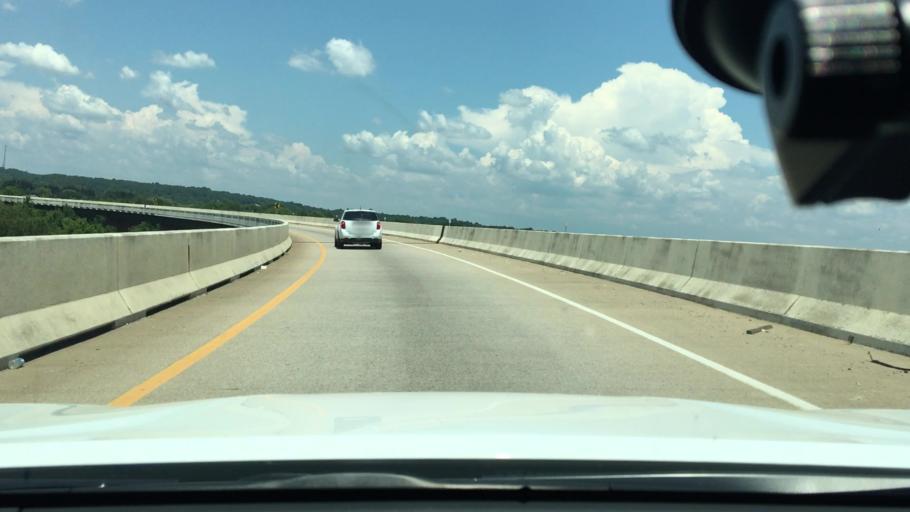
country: US
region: Arkansas
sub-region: Crawford County
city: Alma
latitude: 35.4820
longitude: -94.2422
